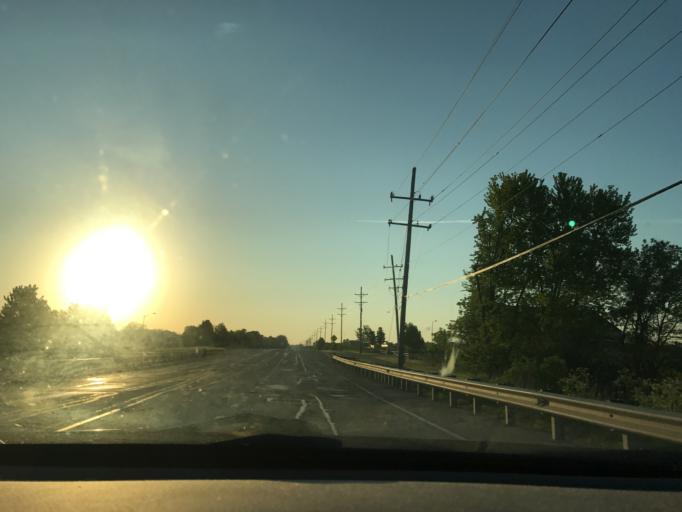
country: US
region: Illinois
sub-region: Kane County
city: South Elgin
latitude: 42.0068
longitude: -88.3508
